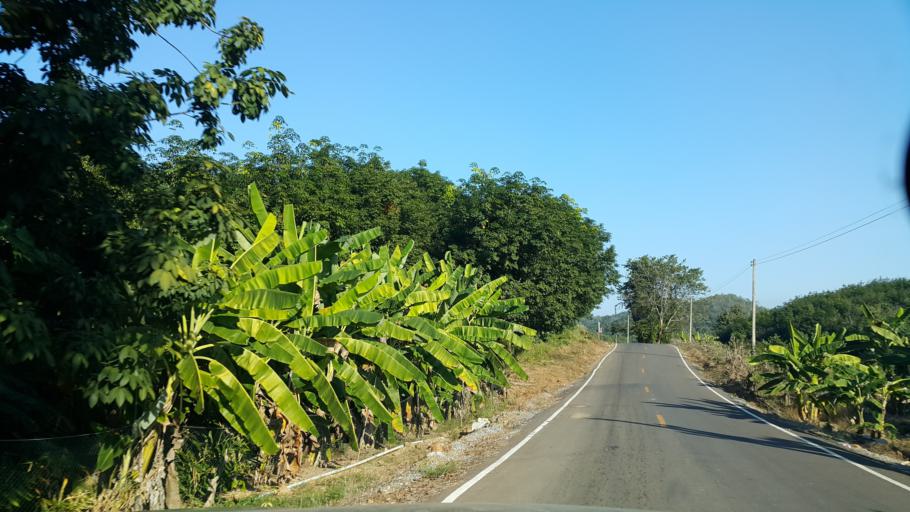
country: TH
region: Sukhothai
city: Thung Saliam
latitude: 17.4010
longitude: 99.5102
